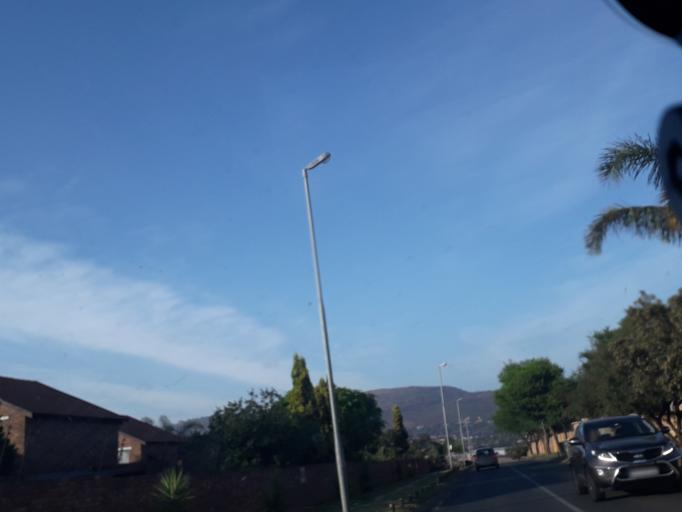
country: ZA
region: Gauteng
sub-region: City of Johannesburg Metropolitan Municipality
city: Roodepoort
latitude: -26.1045
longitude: 27.8955
